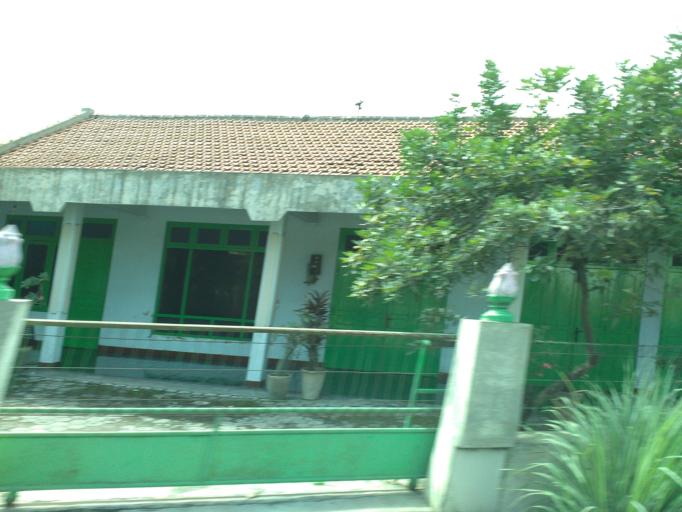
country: ID
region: Central Java
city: Candi Prambanan
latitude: -7.7446
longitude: 110.5279
